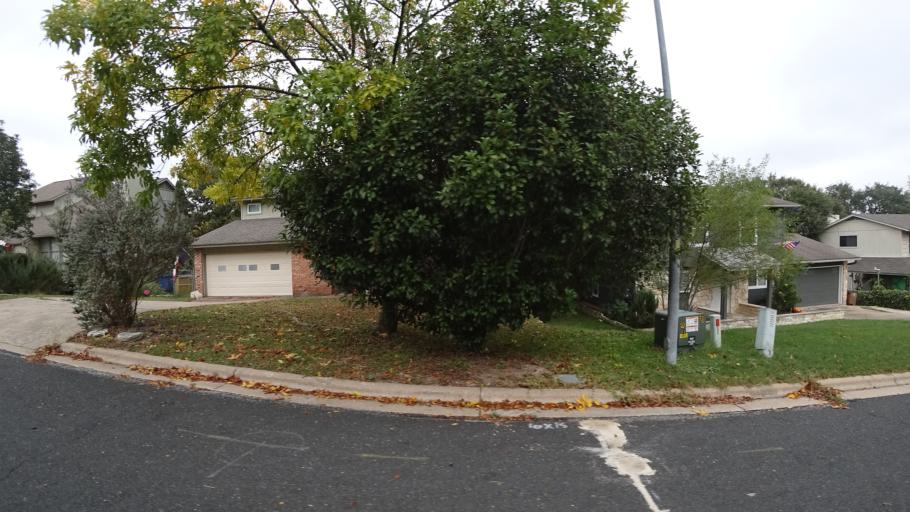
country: US
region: Texas
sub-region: Travis County
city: Barton Creek
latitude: 30.2386
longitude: -97.8960
